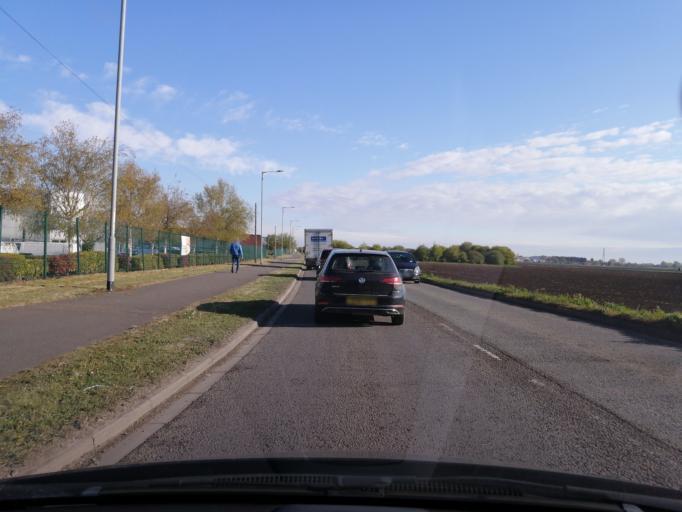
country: GB
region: England
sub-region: Peterborough
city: Eye
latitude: 52.5798
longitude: -0.2040
